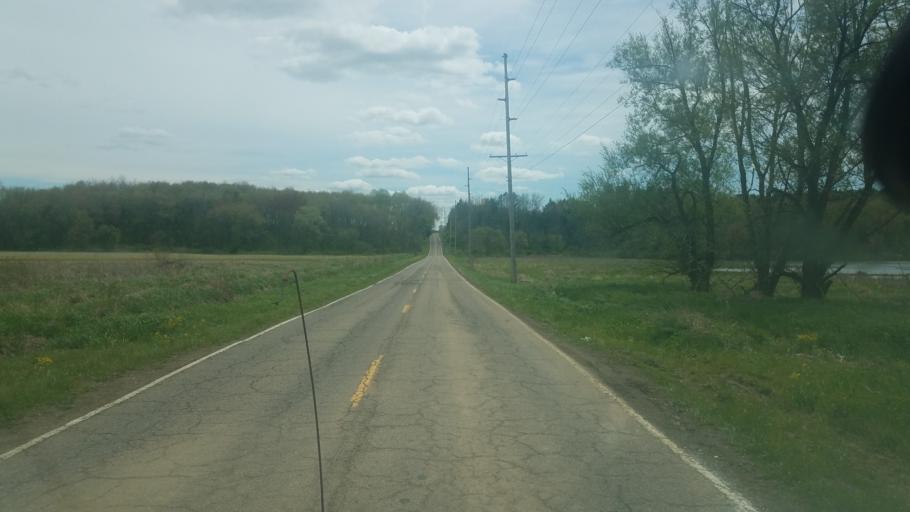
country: US
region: Ohio
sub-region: Wayne County
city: Wooster
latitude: 40.7412
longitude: -81.9442
